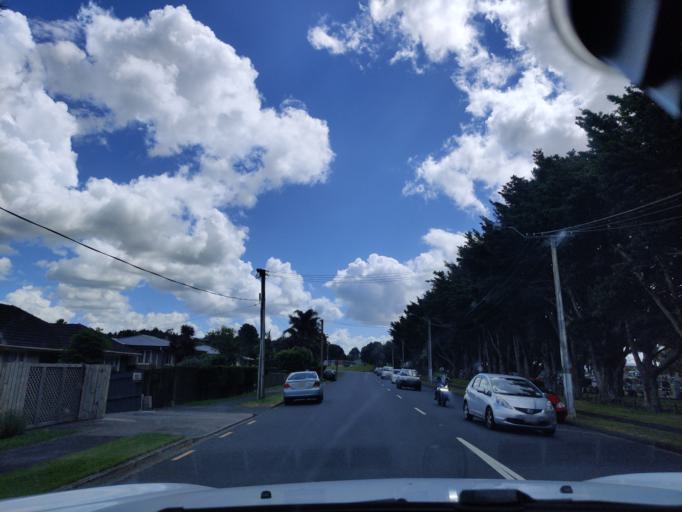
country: NZ
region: Auckland
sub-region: Auckland
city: Papakura
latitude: -37.0702
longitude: 174.9455
